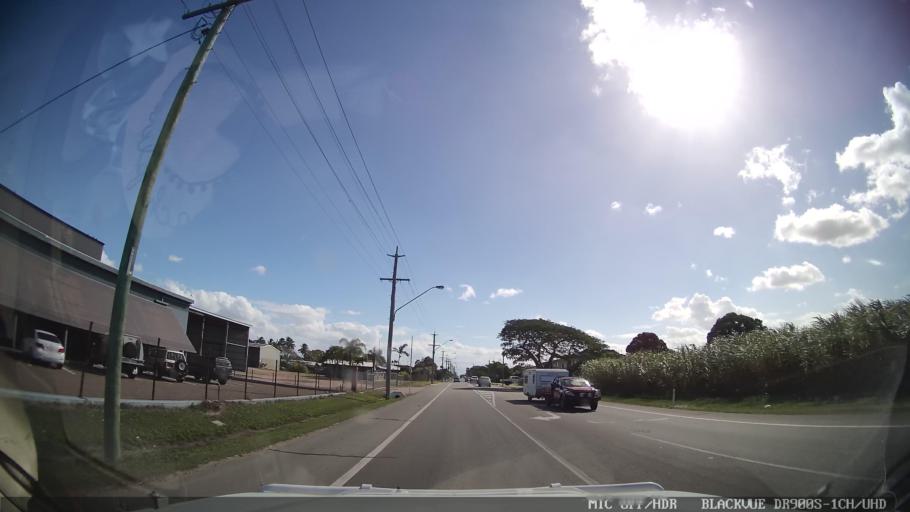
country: AU
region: Queensland
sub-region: Burdekin
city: Ayr
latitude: -19.5551
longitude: 147.3634
